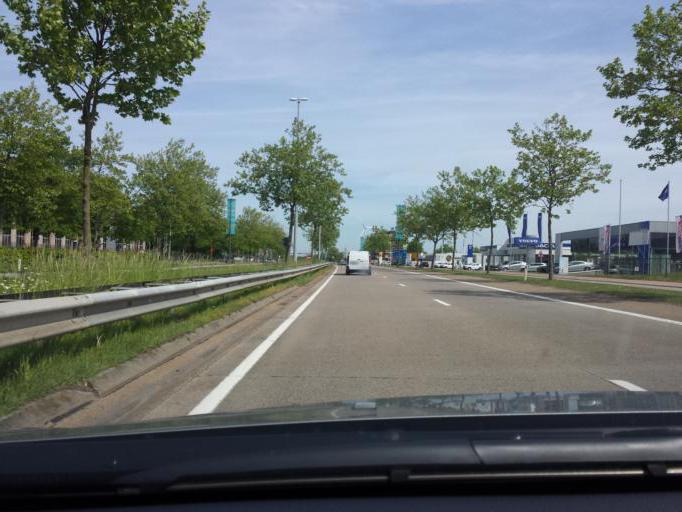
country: BE
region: Flanders
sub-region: Provincie Limburg
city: Hasselt
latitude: 50.9241
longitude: 5.3576
